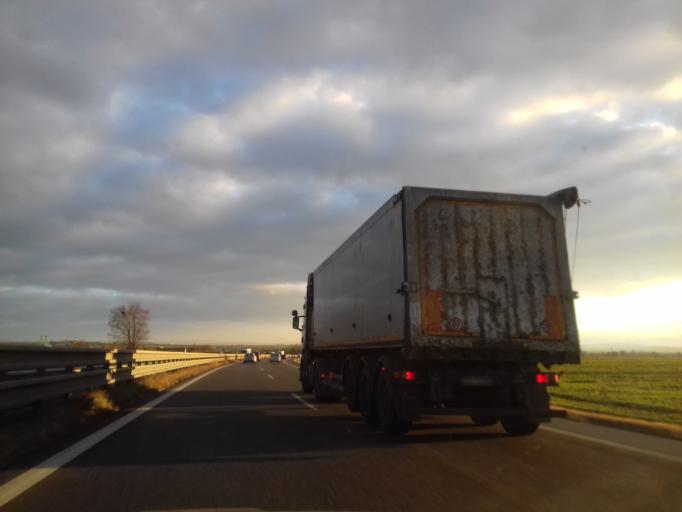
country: CZ
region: Olomoucky
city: Lutin
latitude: 49.5259
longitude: 17.1567
